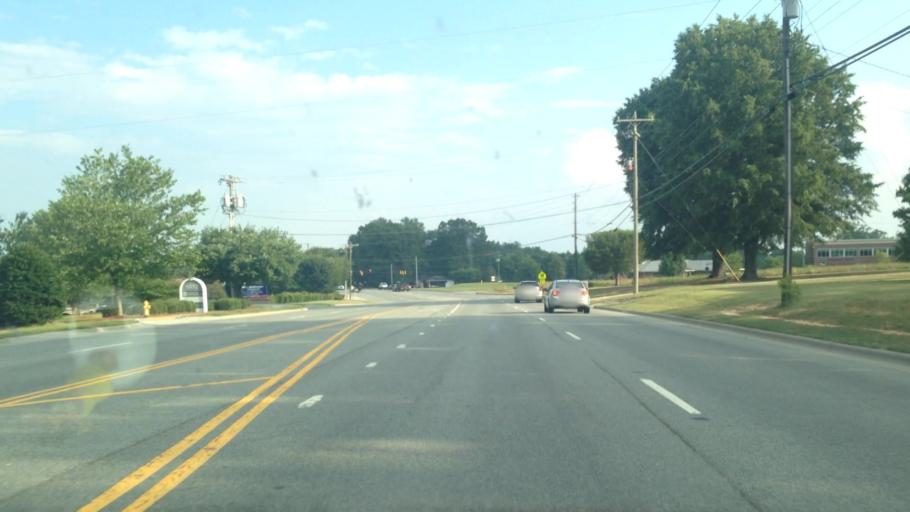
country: US
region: North Carolina
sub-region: Forsyth County
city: Kernersville
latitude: 36.0821
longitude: -80.0640
